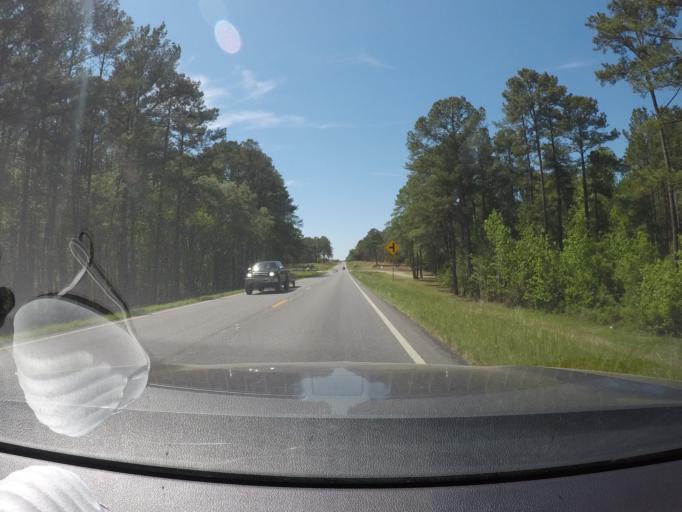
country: US
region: Georgia
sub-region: Evans County
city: Claxton
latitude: 32.1500
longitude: -81.7910
